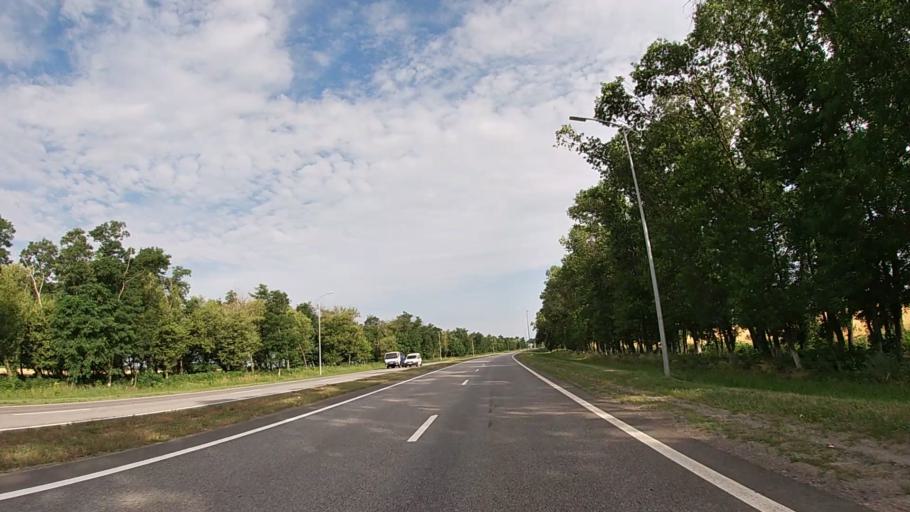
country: RU
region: Belgorod
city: Tomarovka
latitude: 50.6735
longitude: 36.2969
